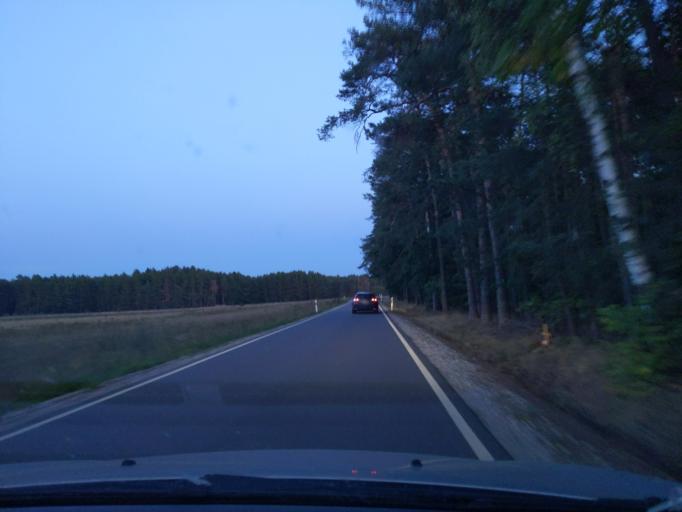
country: DE
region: Saxony
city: Lohsa
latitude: 51.3298
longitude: 14.3953
